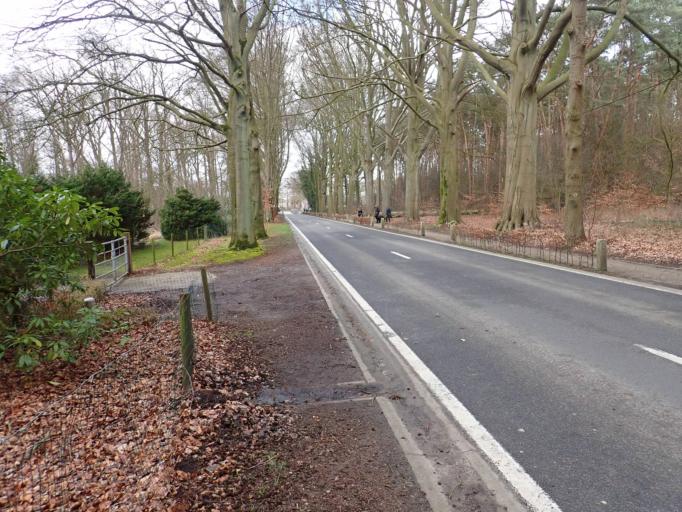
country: BE
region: Flanders
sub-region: Provincie Antwerpen
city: Schilde
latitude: 51.2835
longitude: 4.5704
